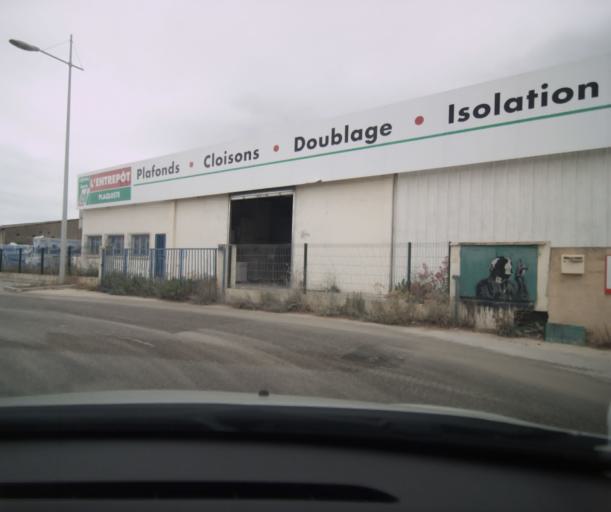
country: FR
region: Provence-Alpes-Cote d'Azur
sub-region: Departement du Var
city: La Farlede
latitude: 43.1401
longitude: 6.0366
